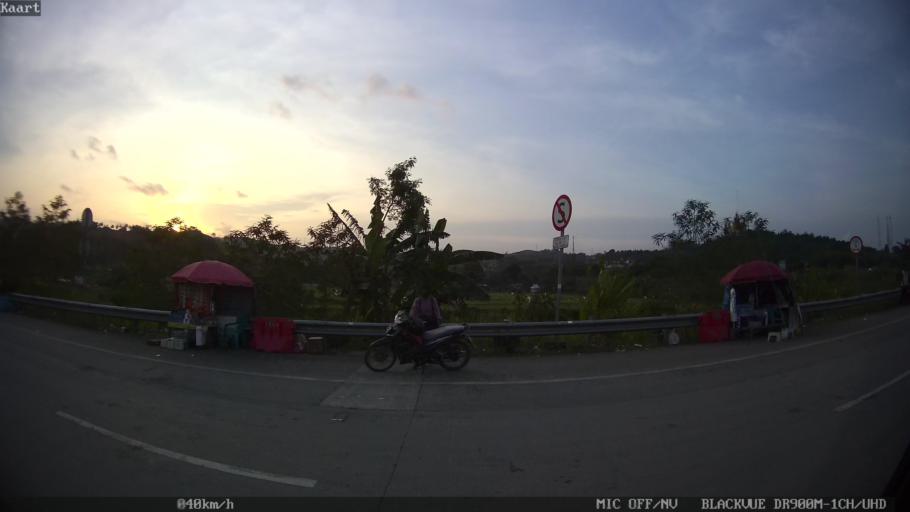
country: ID
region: Lampung
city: Penengahan
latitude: -5.8705
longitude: 105.7508
